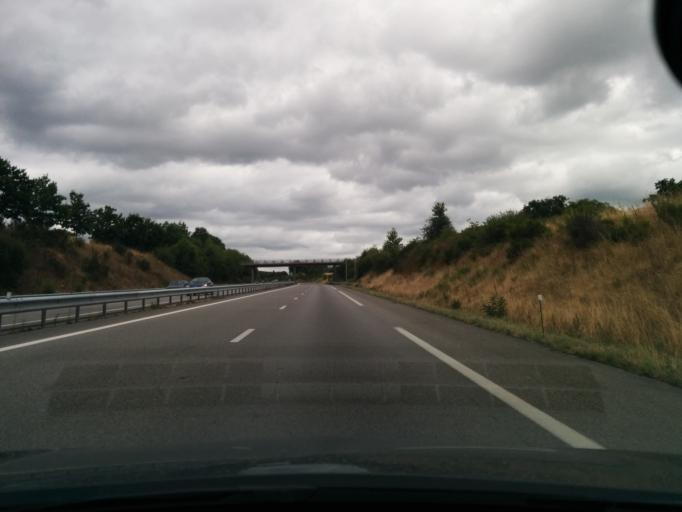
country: FR
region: Limousin
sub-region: Departement de la Haute-Vienne
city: Saint-Sulpice-les-Feuilles
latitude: 46.3449
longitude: 1.4227
